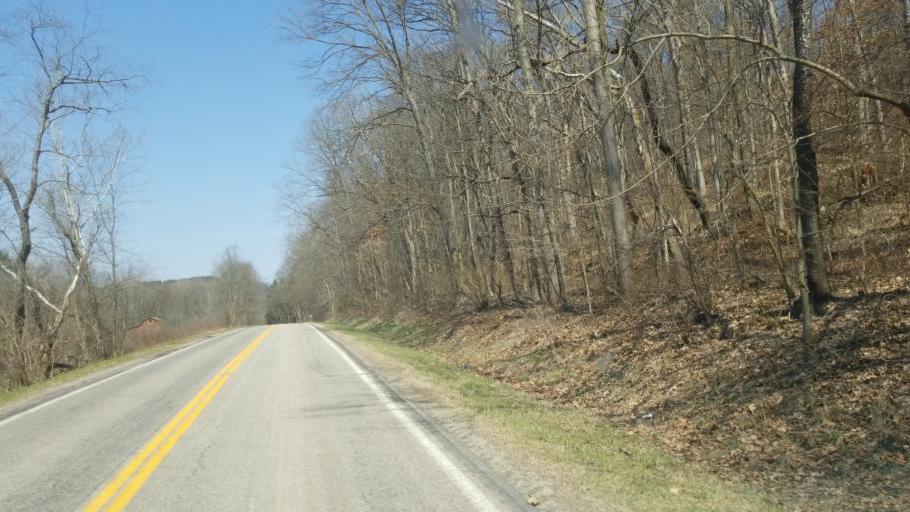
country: US
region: Ohio
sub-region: Ashland County
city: Loudonville
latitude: 40.7056
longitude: -82.1586
